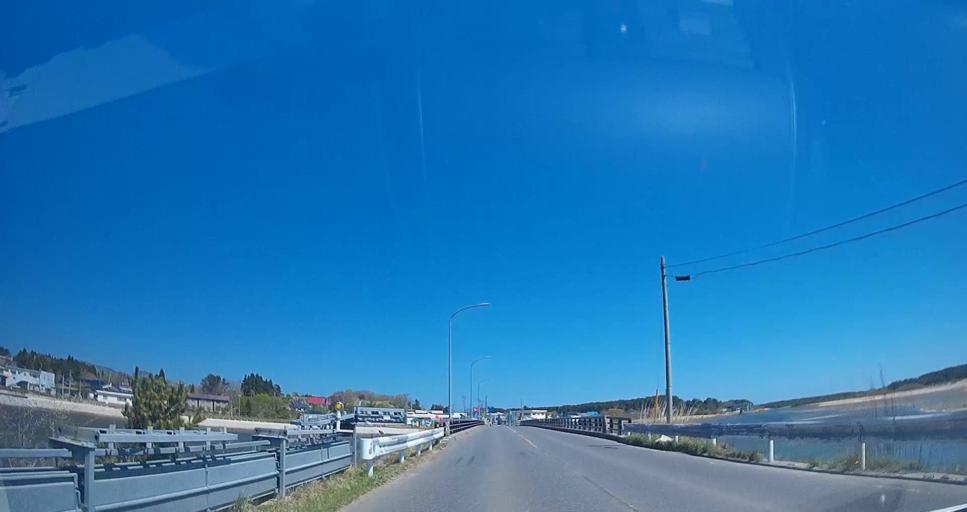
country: JP
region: Aomori
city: Misawa
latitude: 40.9582
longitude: 141.3713
